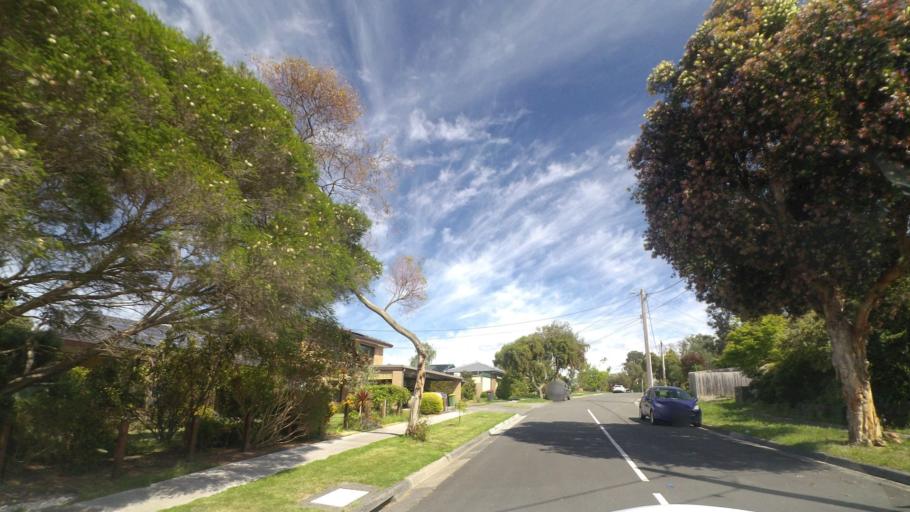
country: AU
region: Victoria
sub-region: Knox
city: Bayswater
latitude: -37.8544
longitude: 145.2523
